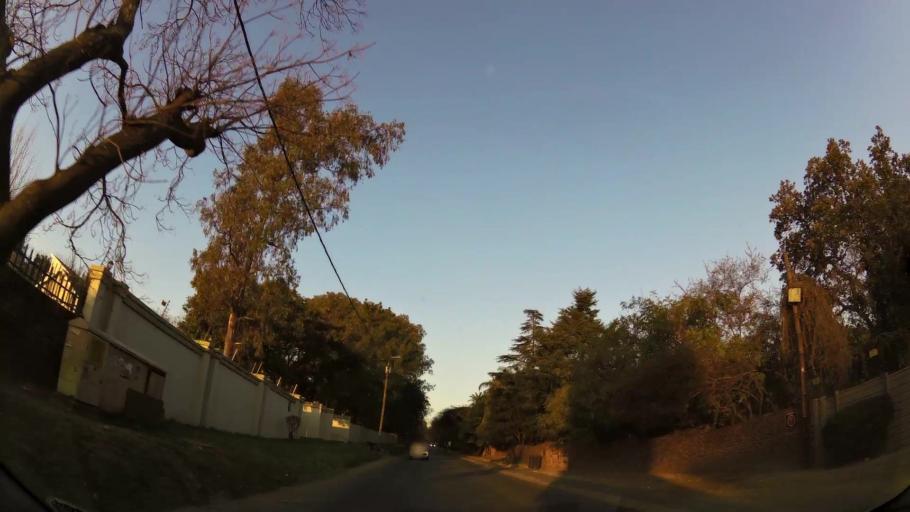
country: ZA
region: Gauteng
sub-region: City of Johannesburg Metropolitan Municipality
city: Johannesburg
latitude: -26.1055
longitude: 27.9952
